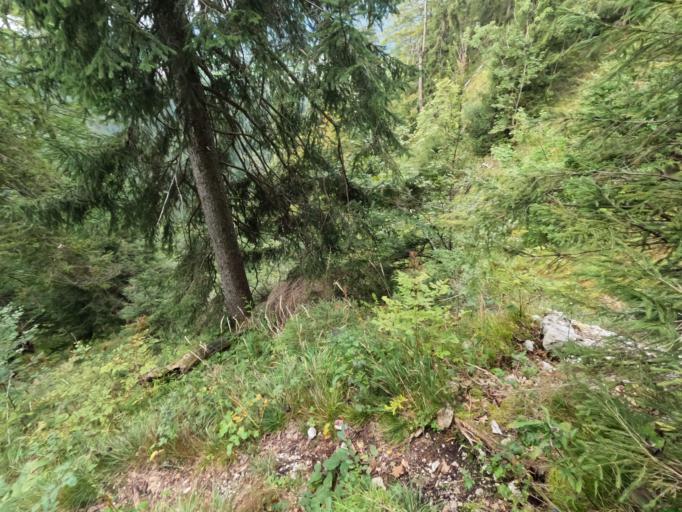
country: DE
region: Bavaria
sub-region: Upper Bavaria
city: Inzell
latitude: 47.7504
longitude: 12.7742
